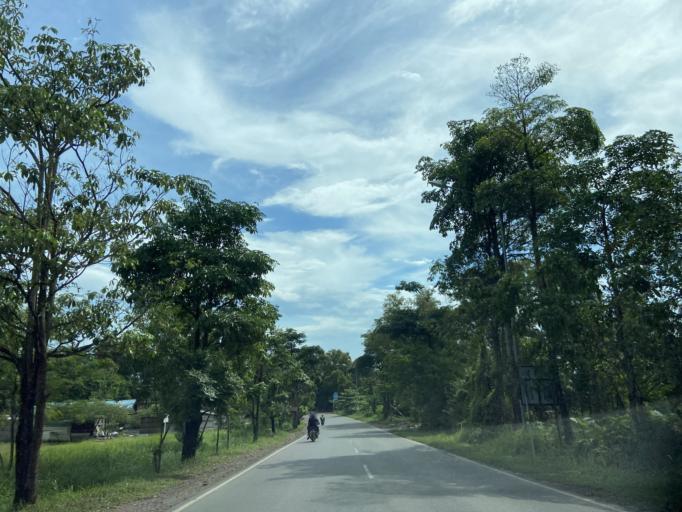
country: SG
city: Singapore
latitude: 1.0536
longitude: 103.9553
